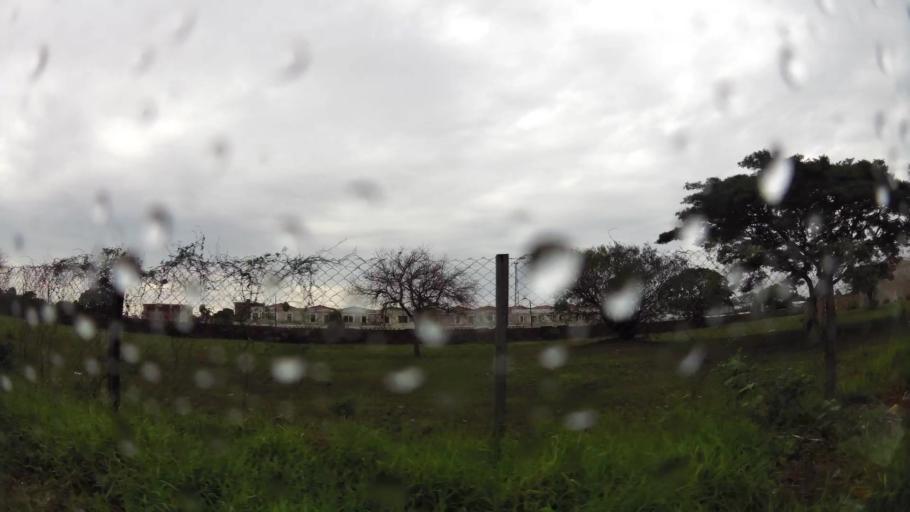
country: BO
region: Santa Cruz
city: Santa Cruz de la Sierra
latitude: -17.8086
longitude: -63.1592
